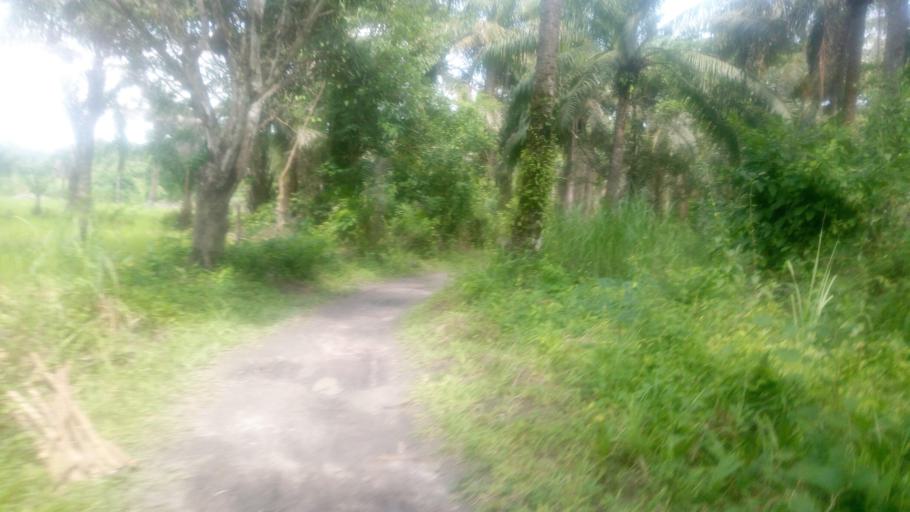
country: SL
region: Northern Province
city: Magburaka
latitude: 8.6675
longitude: -12.0625
